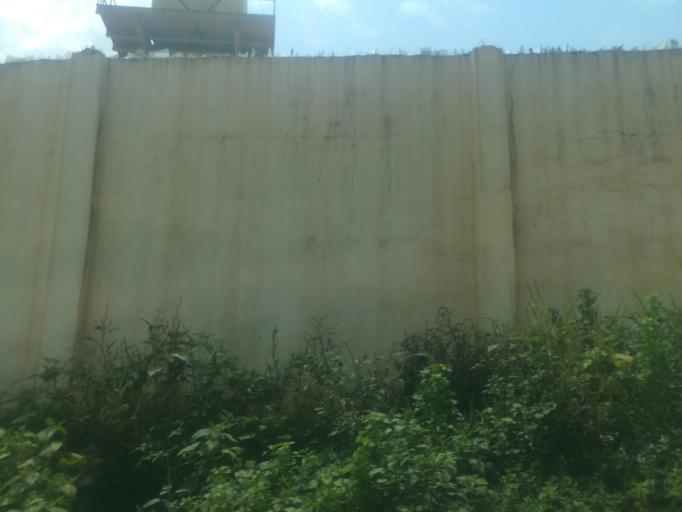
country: NG
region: Oyo
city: Ibadan
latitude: 7.3569
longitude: 3.8426
